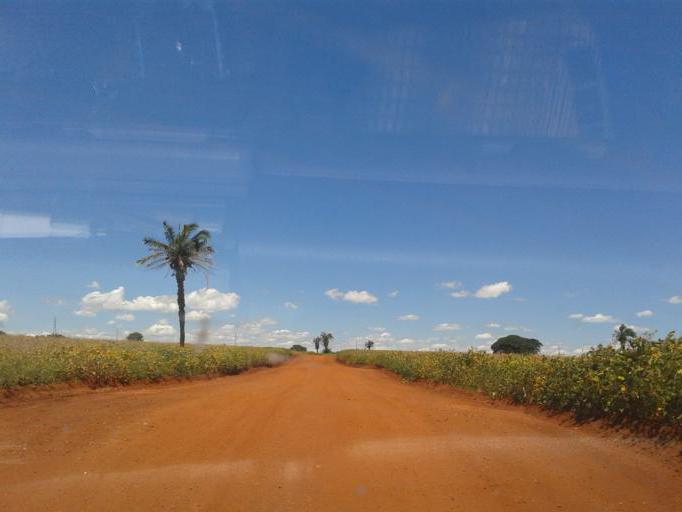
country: BR
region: Minas Gerais
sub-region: Capinopolis
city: Capinopolis
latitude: -18.5721
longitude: -49.5111
